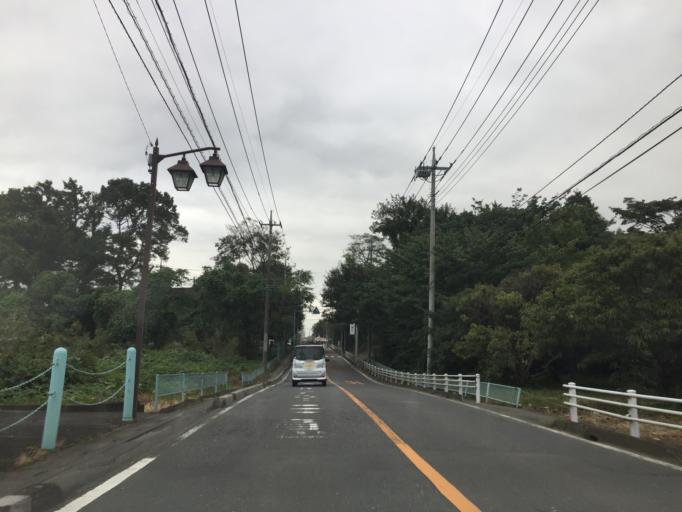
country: JP
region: Saitama
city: Okegawa
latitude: 35.9590
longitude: 139.5572
